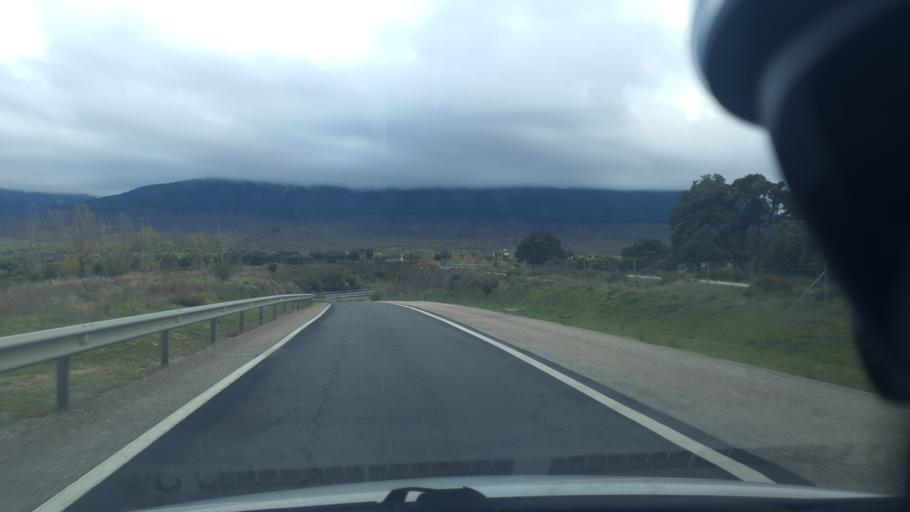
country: ES
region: Castille and Leon
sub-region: Provincia de Segovia
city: Cerezo de Abajo
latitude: 41.2099
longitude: -3.5817
